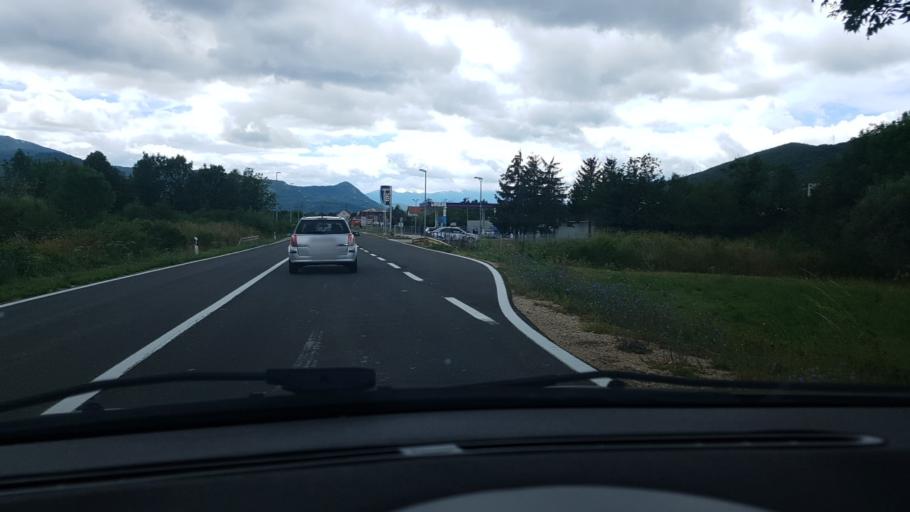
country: HR
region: Zadarska
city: Gracac
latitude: 44.2956
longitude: 15.8487
